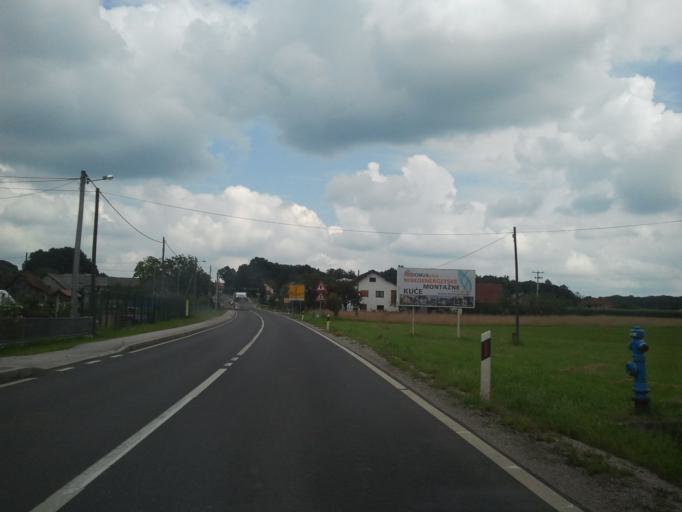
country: HR
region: Grad Zagreb
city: Horvati
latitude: 45.6974
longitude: 15.7619
